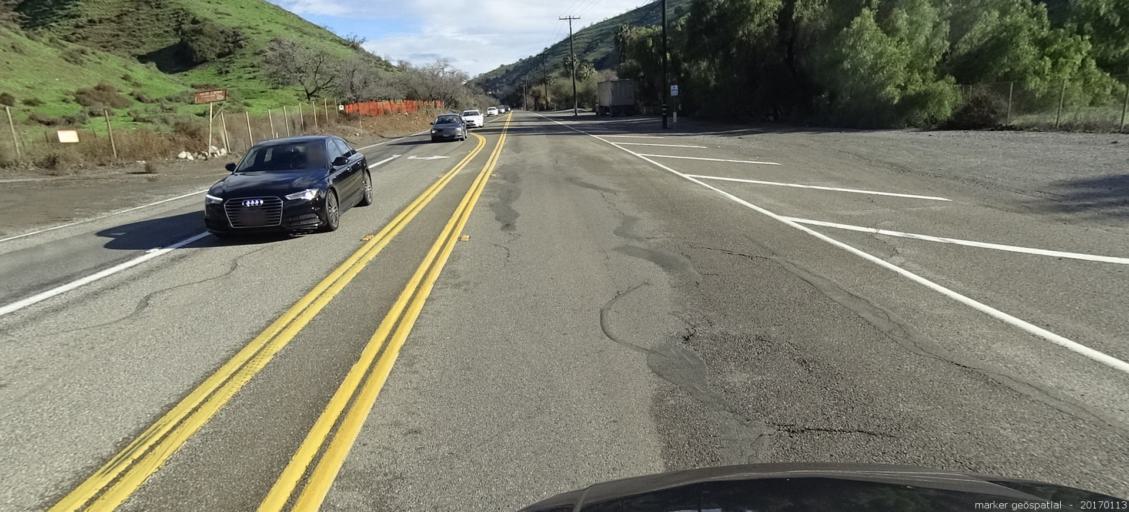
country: US
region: California
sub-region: Orange County
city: Brea
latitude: 33.9434
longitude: -117.8734
